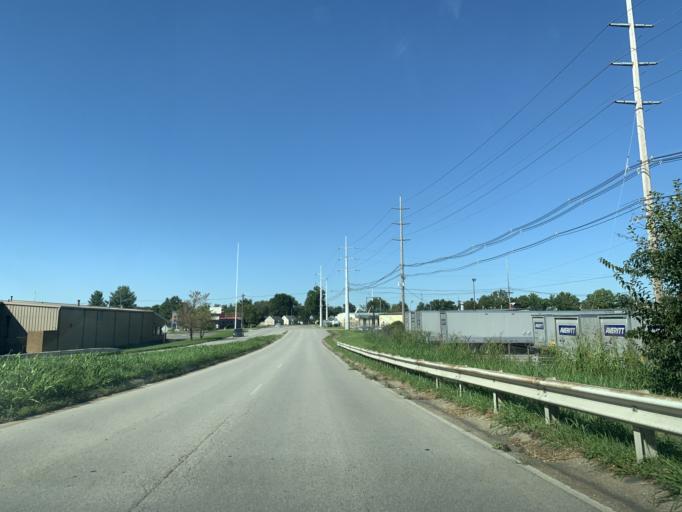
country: US
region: Kentucky
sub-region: Jefferson County
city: West Buechel
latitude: 38.1924
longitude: -85.6662
